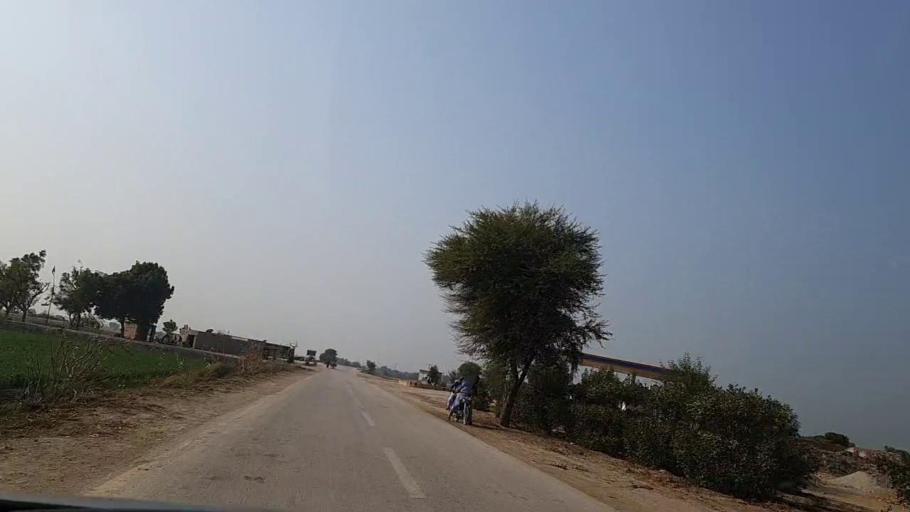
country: PK
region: Sindh
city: Sann
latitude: 26.1443
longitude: 68.1458
